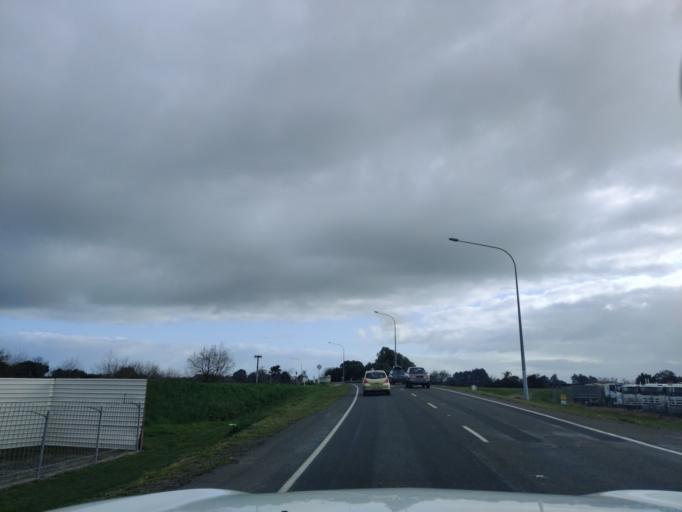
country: NZ
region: Manawatu-Wanganui
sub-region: Palmerston North City
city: Palmerston North
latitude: -40.3371
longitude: 175.5947
